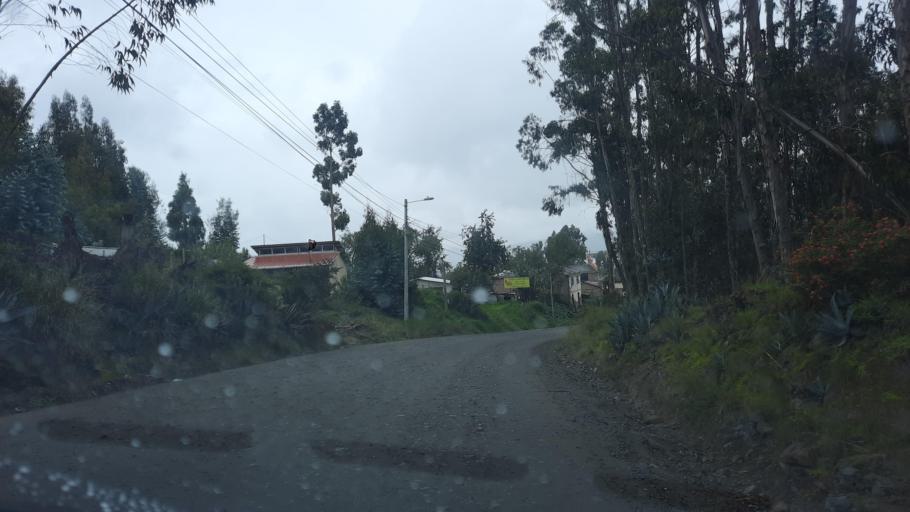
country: EC
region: Chimborazo
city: Riobamba
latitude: -1.6881
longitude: -78.6555
